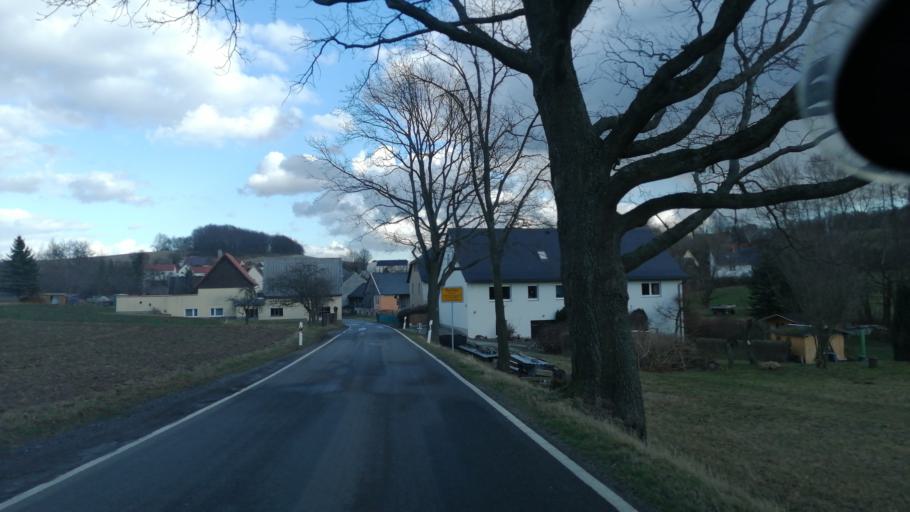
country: DE
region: Saxony
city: Kubschutz
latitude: 51.1367
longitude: 14.5096
